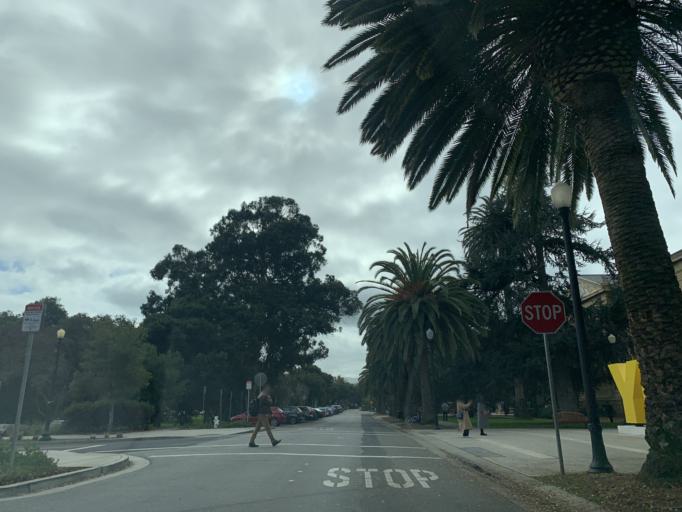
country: US
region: California
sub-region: Santa Clara County
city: Stanford
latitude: 37.4331
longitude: -122.1702
